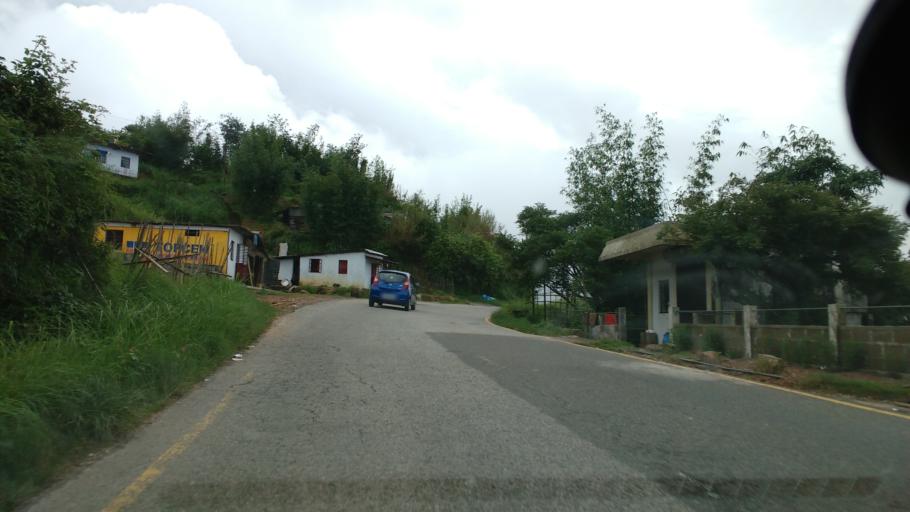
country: IN
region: Meghalaya
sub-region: East Khasi Hills
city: Cherrapunji
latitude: 25.2811
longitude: 91.7297
